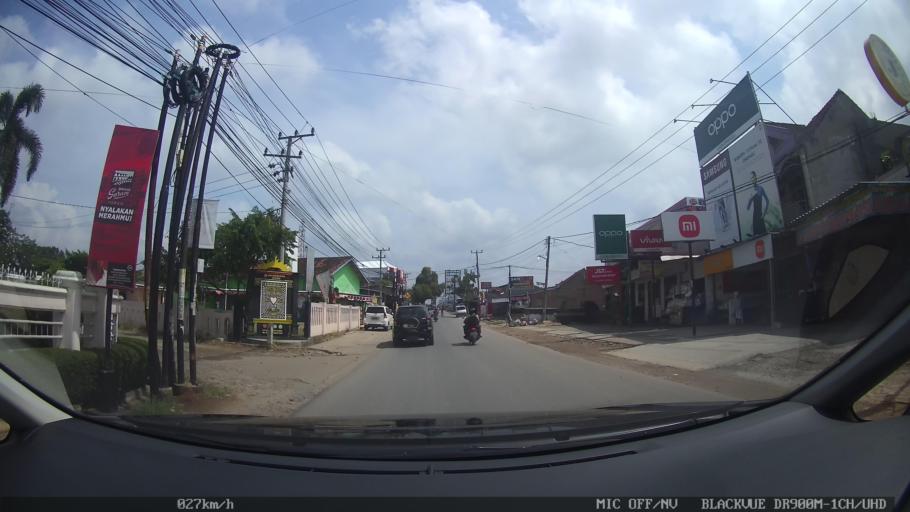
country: ID
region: Lampung
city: Kedaton
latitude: -5.3406
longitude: 105.2937
